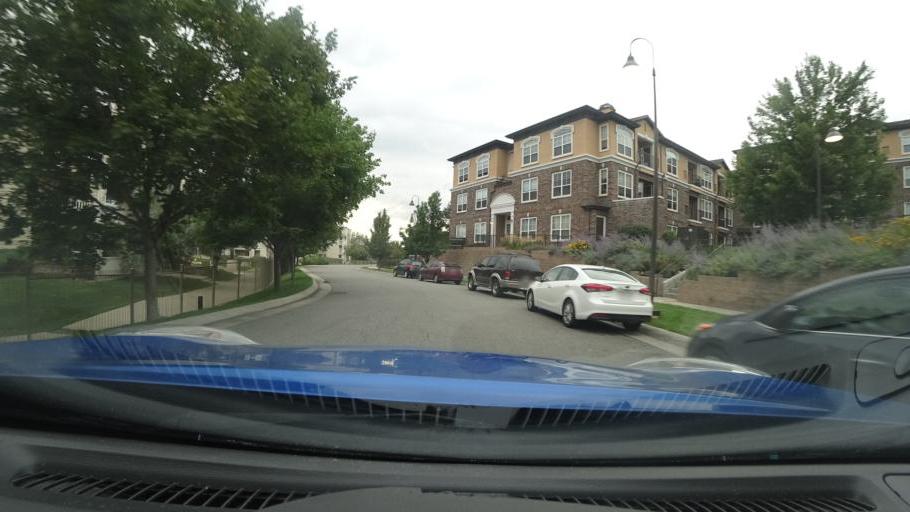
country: US
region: Colorado
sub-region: Adams County
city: Aurora
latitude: 39.7006
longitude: -104.8210
